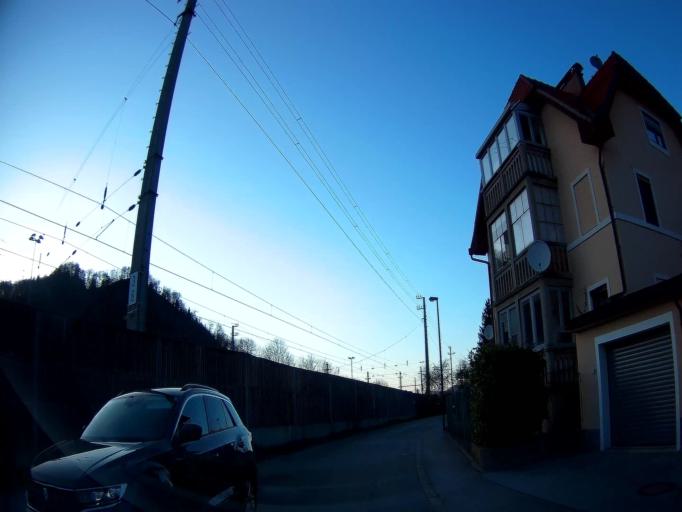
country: TN
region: Qibili
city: Douz
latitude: 33.4635
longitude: 9.1493
